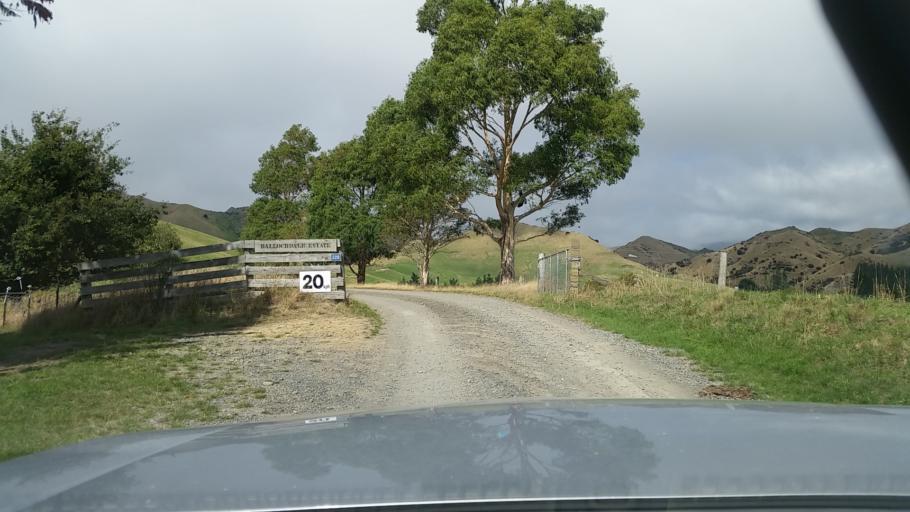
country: NZ
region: Marlborough
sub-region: Marlborough District
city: Blenheim
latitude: -41.7529
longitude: 173.8969
